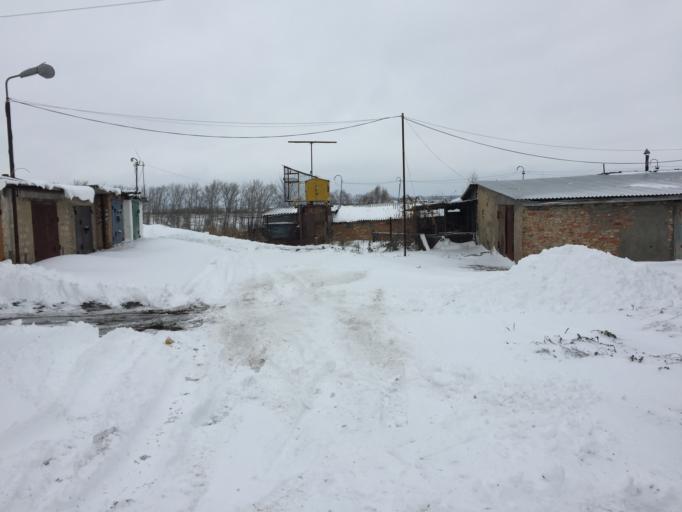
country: RU
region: Tula
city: Shchekino
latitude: 53.8540
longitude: 37.4767
